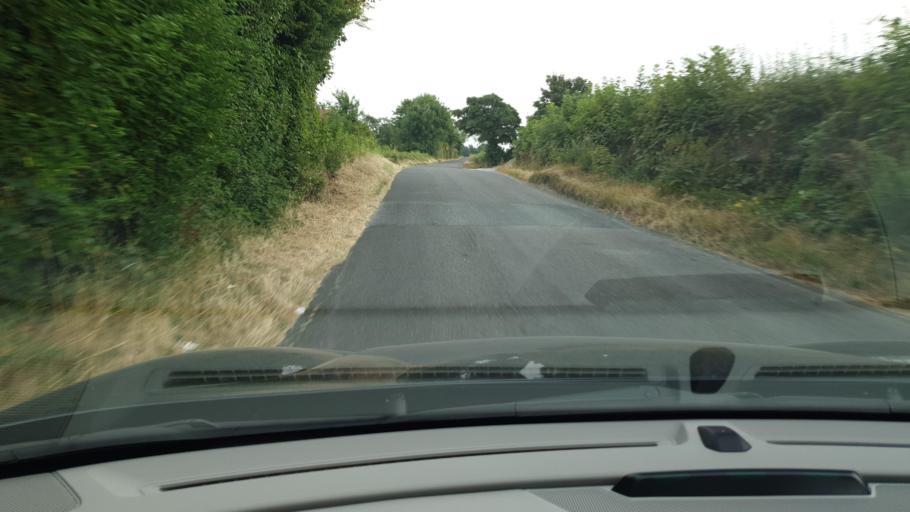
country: IE
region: Leinster
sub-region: An Mhi
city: Ashbourne
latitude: 53.4978
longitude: -6.3726
